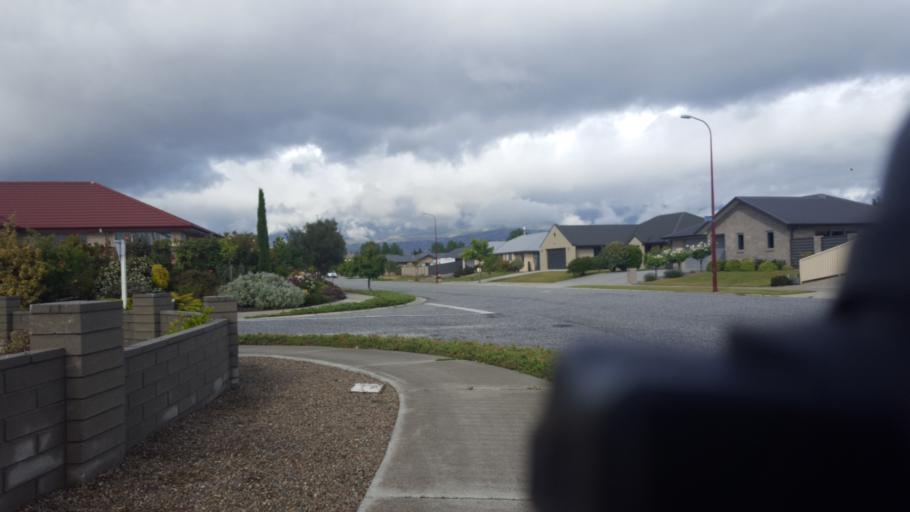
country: NZ
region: Otago
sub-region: Queenstown-Lakes District
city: Wanaka
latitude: -45.2393
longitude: 169.3807
